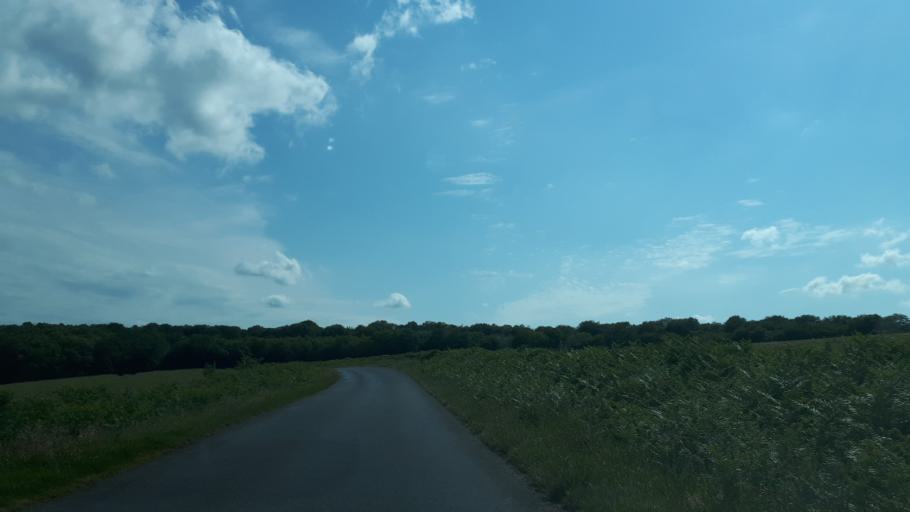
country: FR
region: Centre
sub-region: Departement du Cher
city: Henrichemont
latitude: 47.4000
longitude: 2.5954
